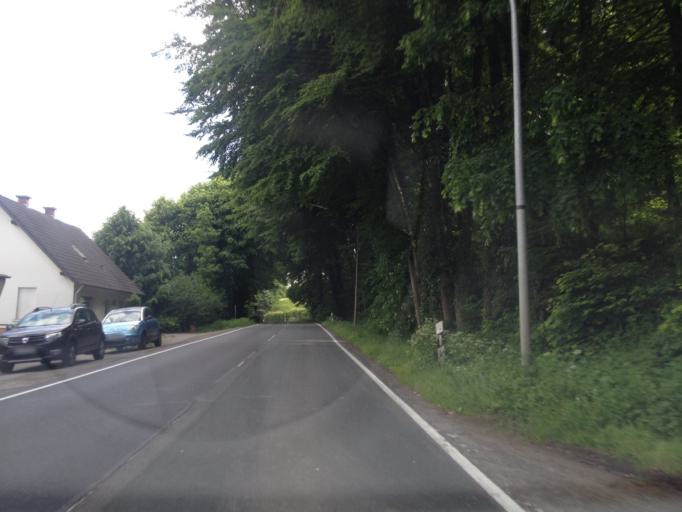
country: DE
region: North Rhine-Westphalia
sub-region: Regierungsbezirk Detmold
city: Rodinghausen
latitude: 52.2647
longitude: 8.5182
